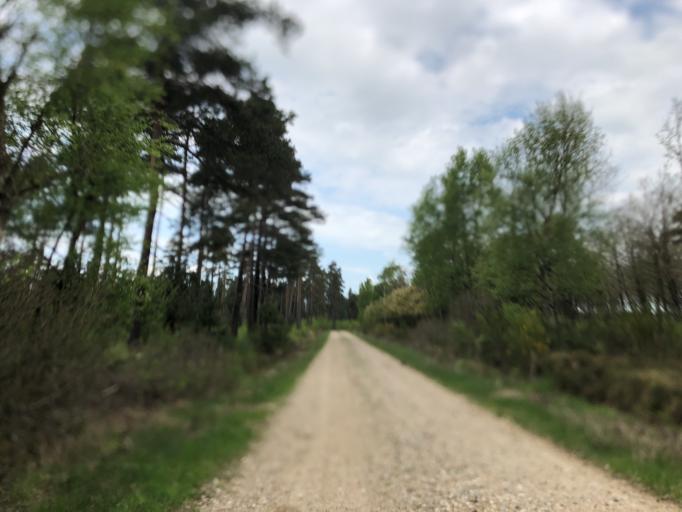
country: DK
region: Central Jutland
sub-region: Holstebro Kommune
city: Ulfborg
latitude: 56.2794
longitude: 8.4336
